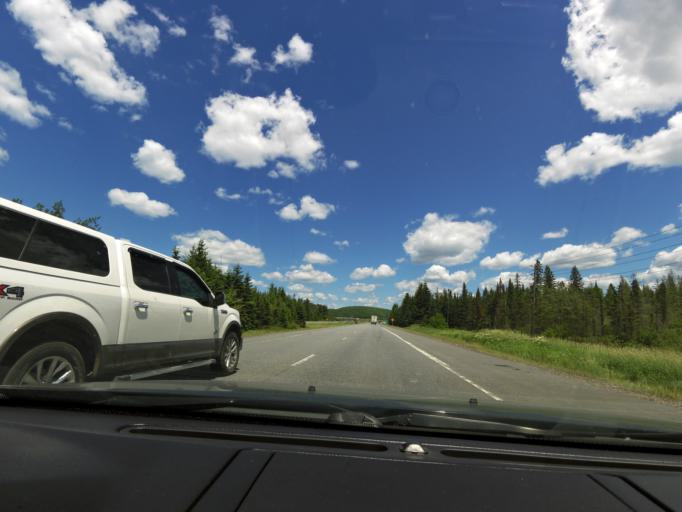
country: CA
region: Ontario
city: Huntsville
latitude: 45.3639
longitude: -79.2182
